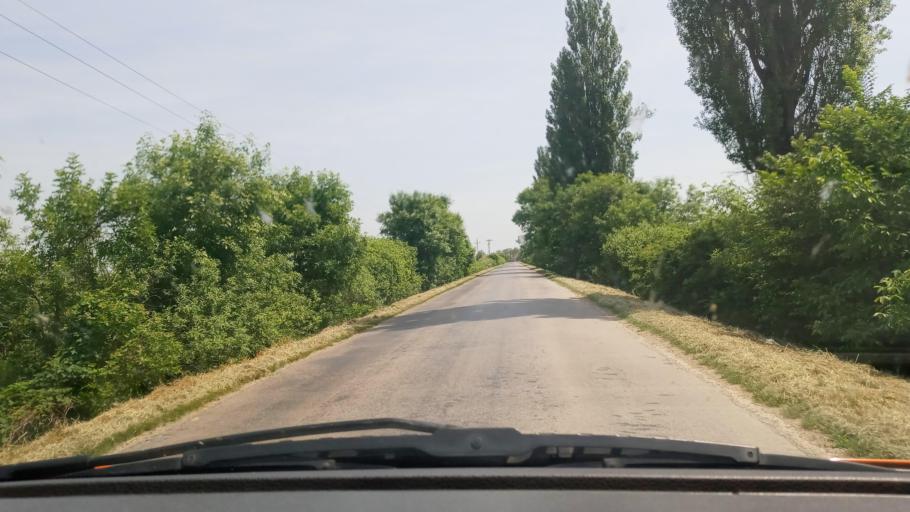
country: HU
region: Baranya
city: Szigetvar
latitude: 45.9655
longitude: 17.7029
